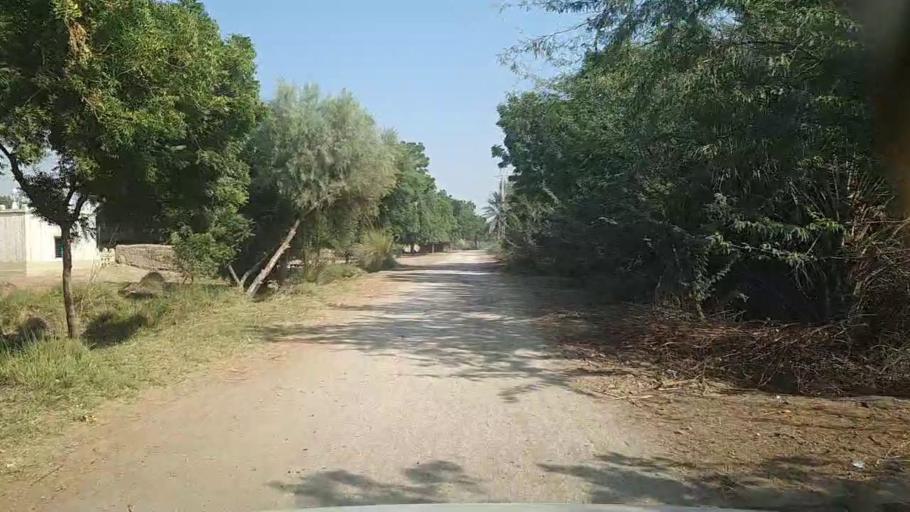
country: PK
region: Sindh
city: Kandiari
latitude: 26.9407
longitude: 68.5408
